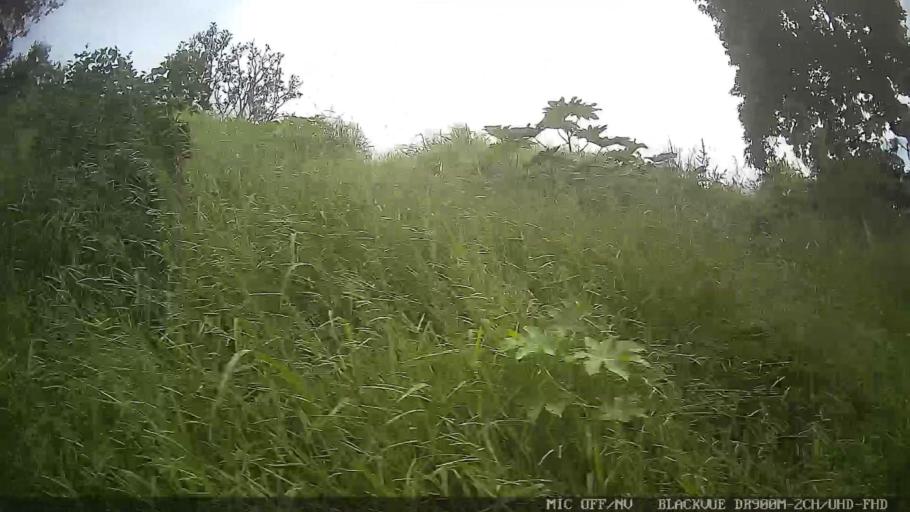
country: BR
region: Minas Gerais
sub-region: Extrema
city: Extrema
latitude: -22.8177
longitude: -46.2941
